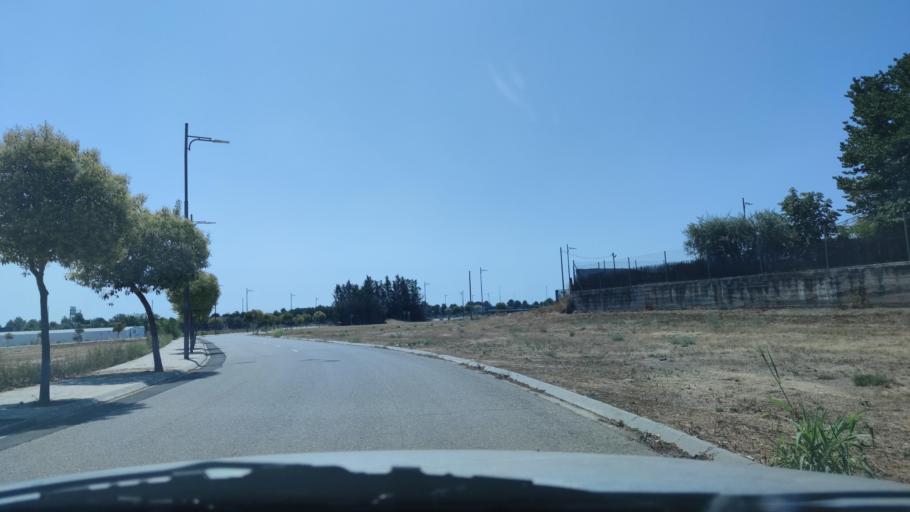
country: ES
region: Catalonia
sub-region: Provincia de Lleida
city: Alpicat
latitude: 41.6504
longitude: 0.5632
